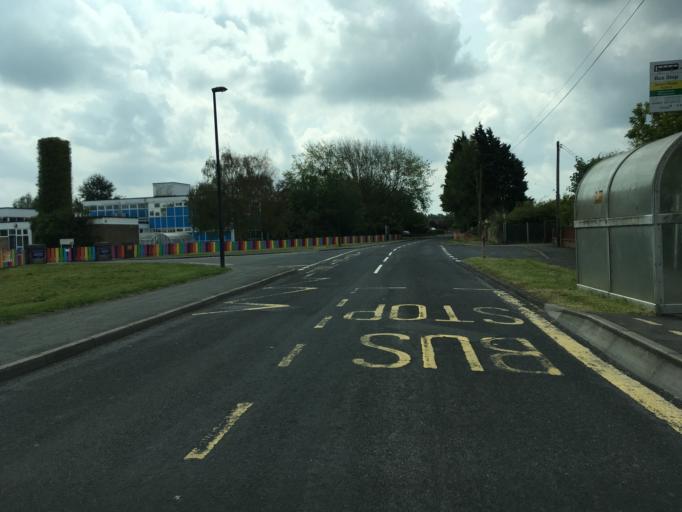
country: GB
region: England
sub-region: South Gloucestershire
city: Severn Beach
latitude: 51.5592
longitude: -2.6619
